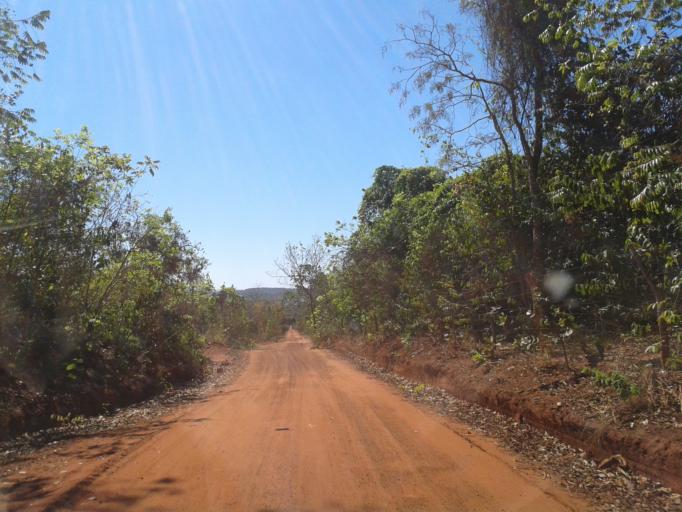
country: BR
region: Minas Gerais
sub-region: Ituiutaba
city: Ituiutaba
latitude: -19.0746
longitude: -49.3164
